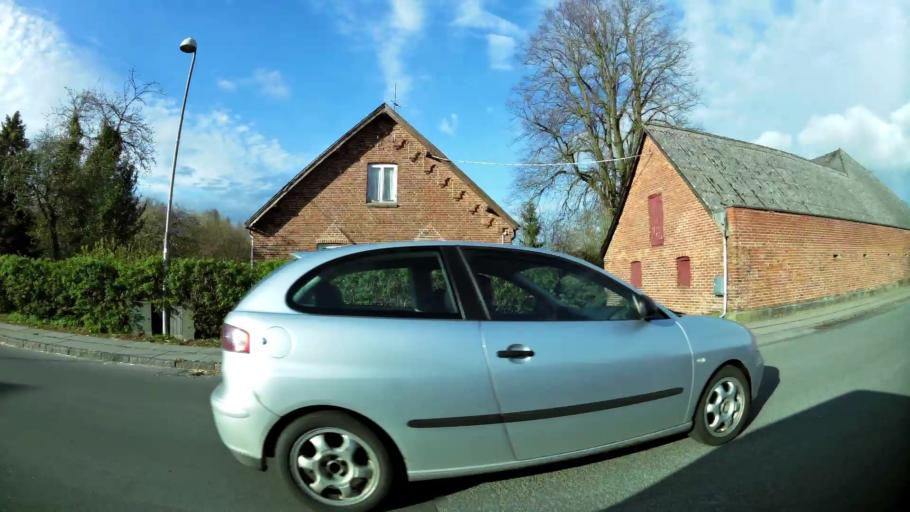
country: DK
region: Central Jutland
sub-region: Syddjurs Kommune
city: Ronde
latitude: 56.3433
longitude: 10.4604
